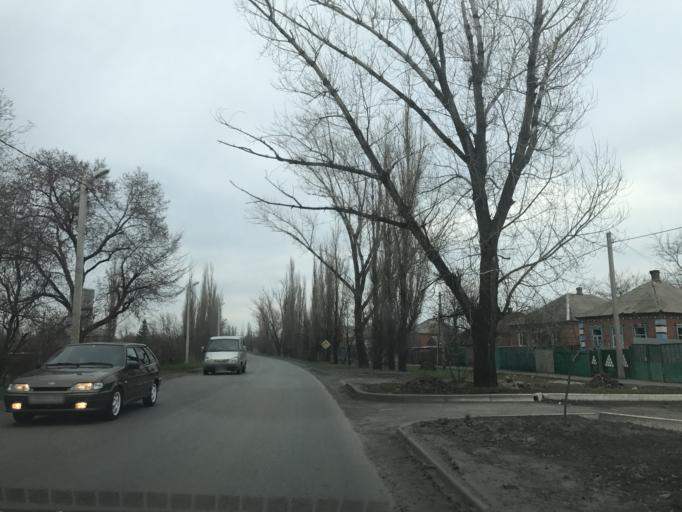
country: RU
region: Rostov
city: Shakhty
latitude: 47.7430
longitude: 40.3241
